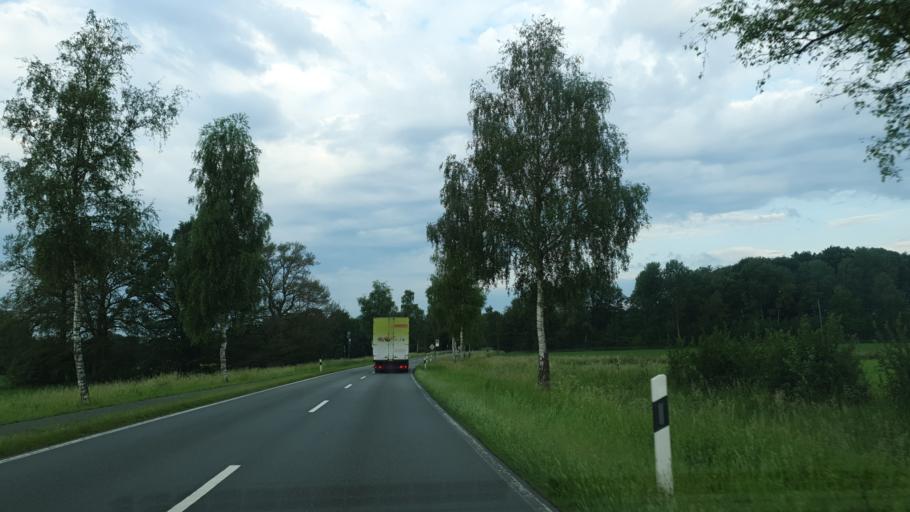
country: DE
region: North Rhine-Westphalia
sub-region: Regierungsbezirk Munster
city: Ostbevern
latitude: 52.0289
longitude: 7.8144
